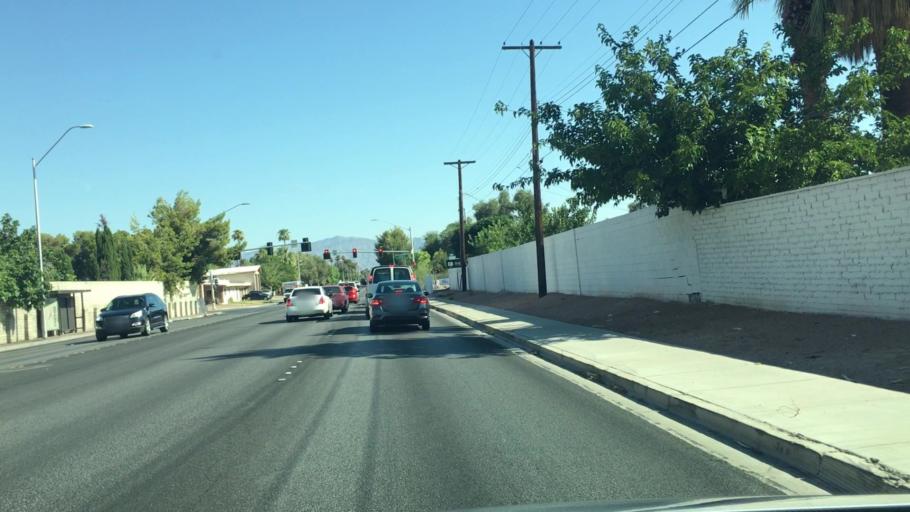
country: US
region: Nevada
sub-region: Clark County
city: Las Vegas
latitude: 36.1506
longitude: -115.1729
